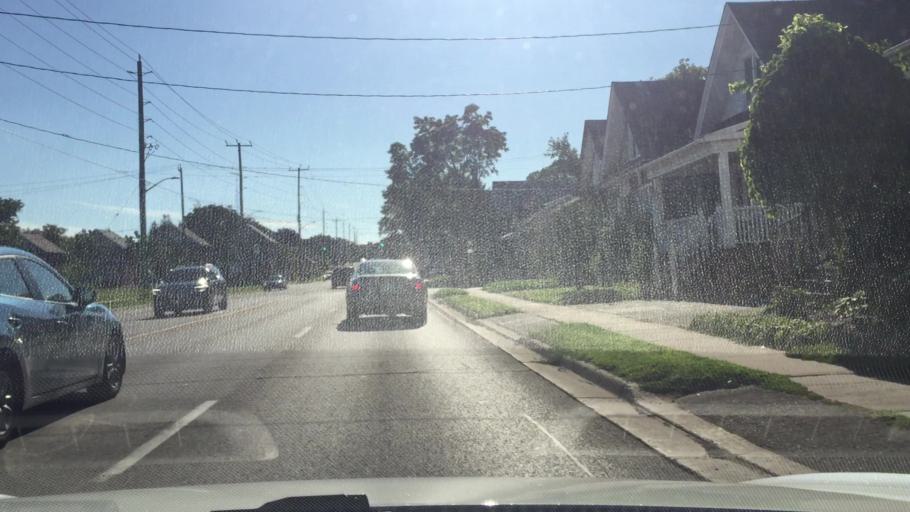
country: CA
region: Ontario
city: Oshawa
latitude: 43.9060
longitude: -78.8586
